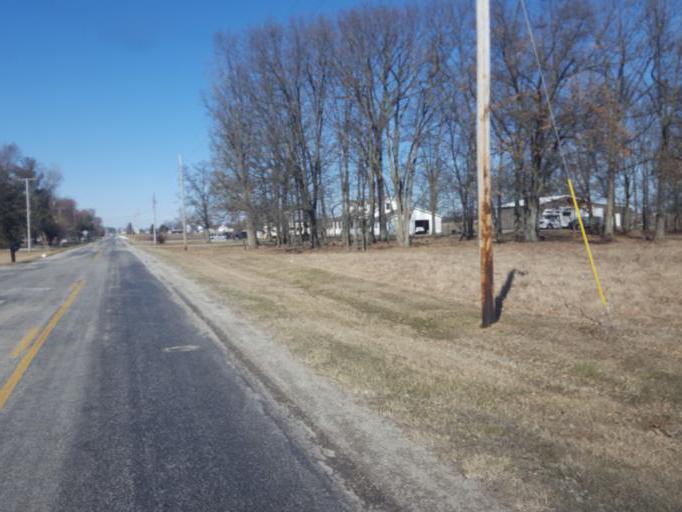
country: US
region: Ohio
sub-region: Marion County
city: Marion
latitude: 40.6521
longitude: -83.0806
